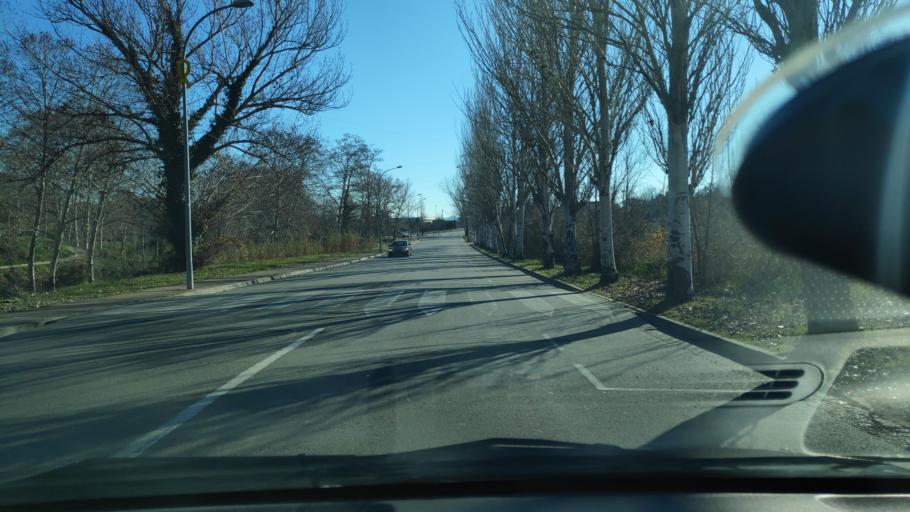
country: ES
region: Catalonia
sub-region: Provincia de Barcelona
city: Sant Quirze del Valles
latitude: 41.5281
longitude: 2.0830
